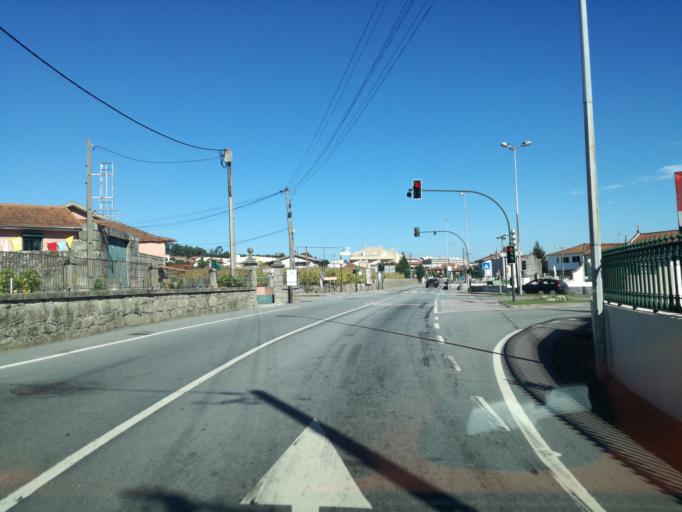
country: PT
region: Porto
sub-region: Trofa
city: Sao Romao do Coronado
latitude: 41.2837
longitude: -8.5682
